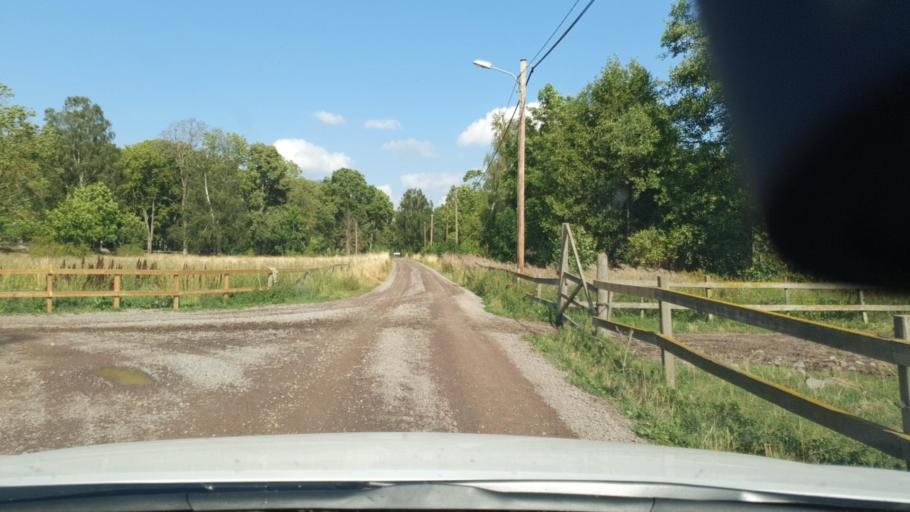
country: SE
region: Kalmar
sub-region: Hultsfreds Kommun
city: Malilla
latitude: 57.3230
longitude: 15.8100
